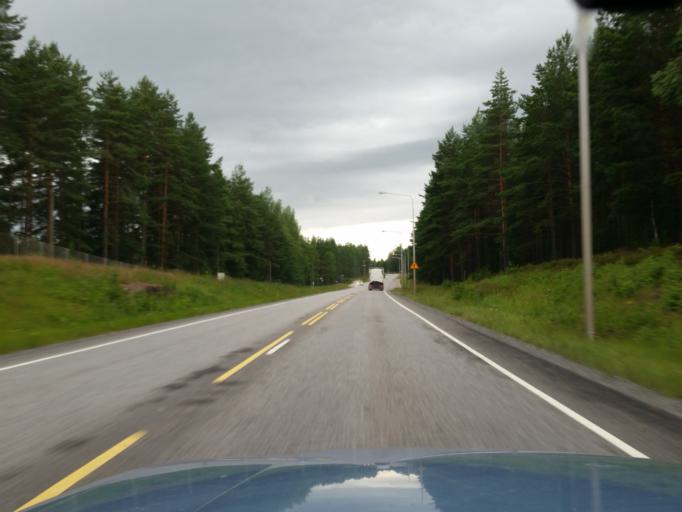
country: FI
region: Uusimaa
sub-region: Raaseporin
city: Ekenaes
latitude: 59.9733
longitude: 23.3913
